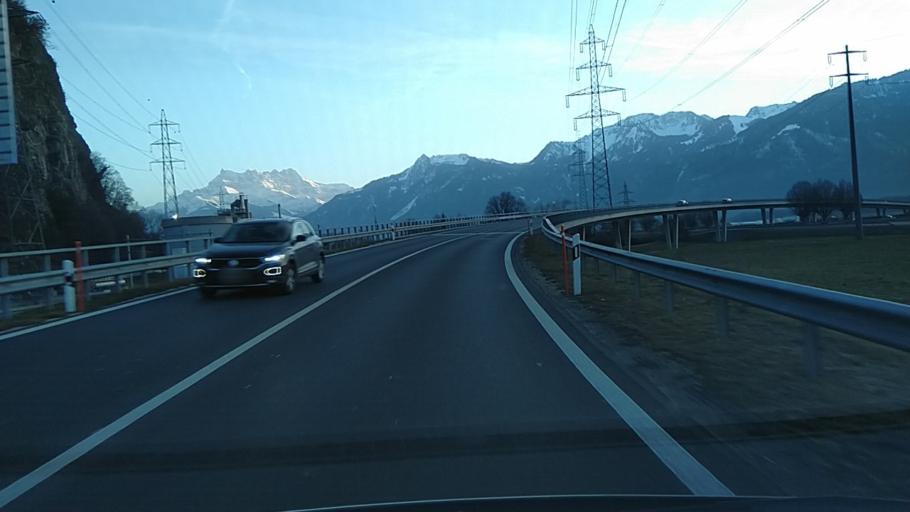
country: CH
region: Vaud
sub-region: Aigle District
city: Villeneuve
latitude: 46.3719
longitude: 6.9250
